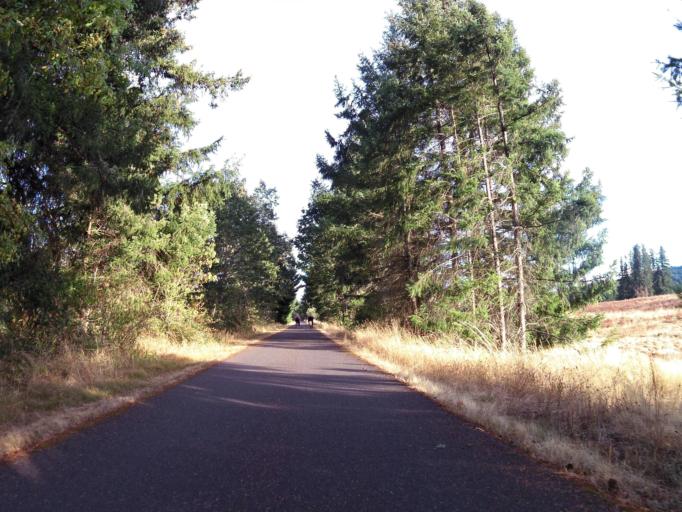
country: US
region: Washington
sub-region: Thurston County
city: Rainier
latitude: 46.8800
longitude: -122.7350
